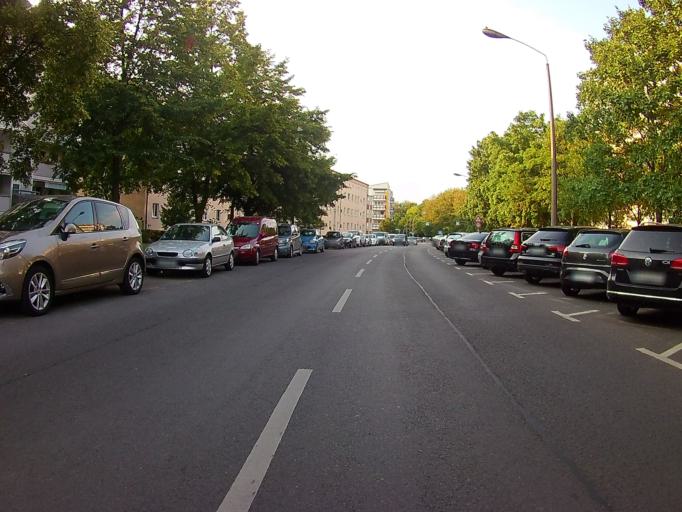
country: DE
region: Berlin
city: Alt-Hohenschoenhausen
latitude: 52.5356
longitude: 13.4996
